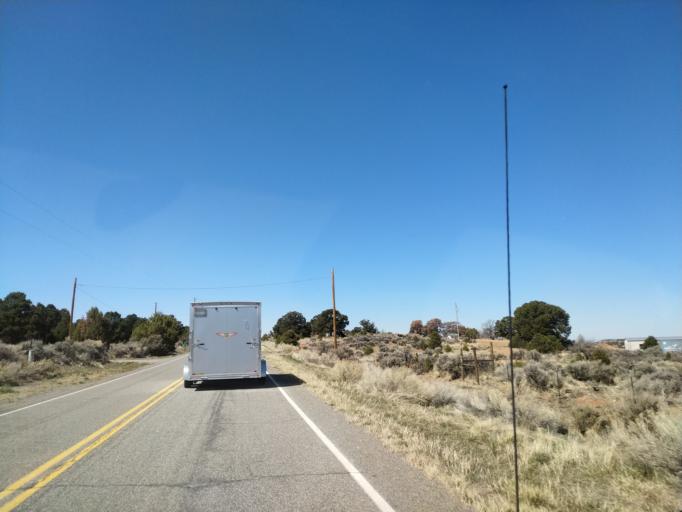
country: US
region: Colorado
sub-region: Mesa County
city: Redlands
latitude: 38.9938
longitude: -108.7254
